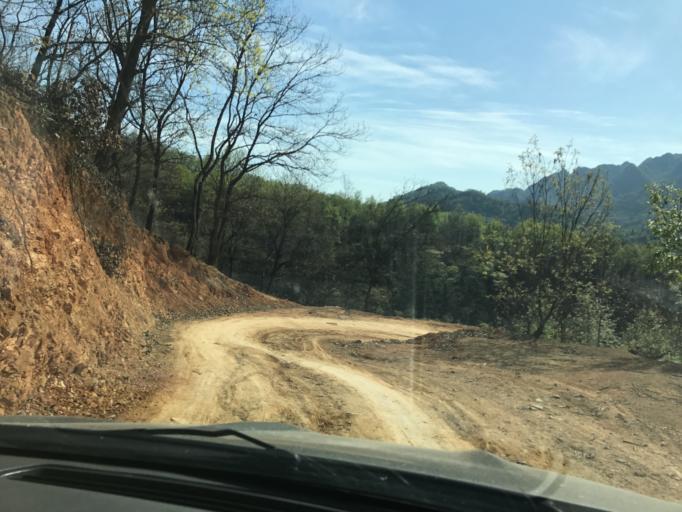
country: CN
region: Guangxi Zhuangzu Zizhiqu
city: Xinzhou
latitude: 25.1061
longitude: 105.8610
